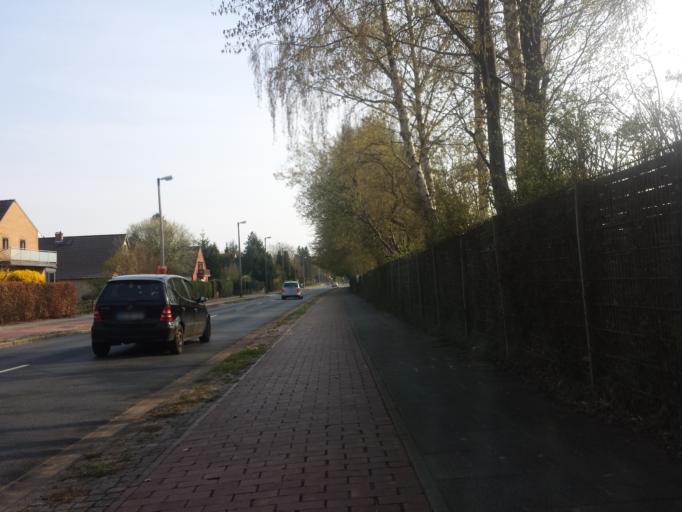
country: DE
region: Lower Saxony
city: Lilienthal
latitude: 53.0735
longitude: 8.9019
